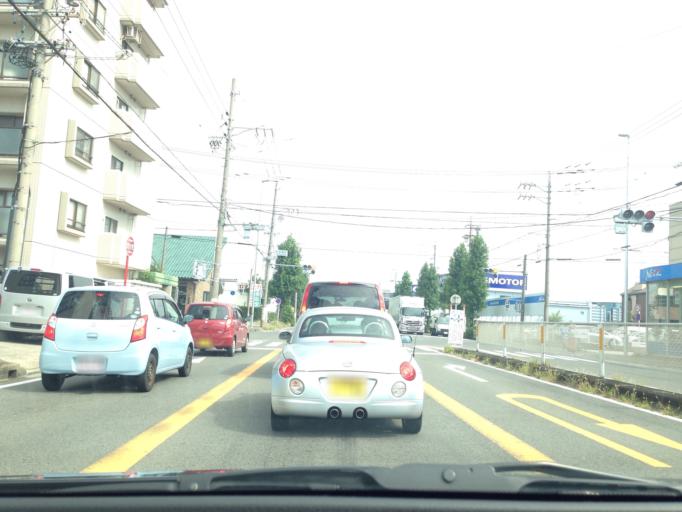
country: JP
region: Aichi
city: Inazawa
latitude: 35.2551
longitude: 136.7792
